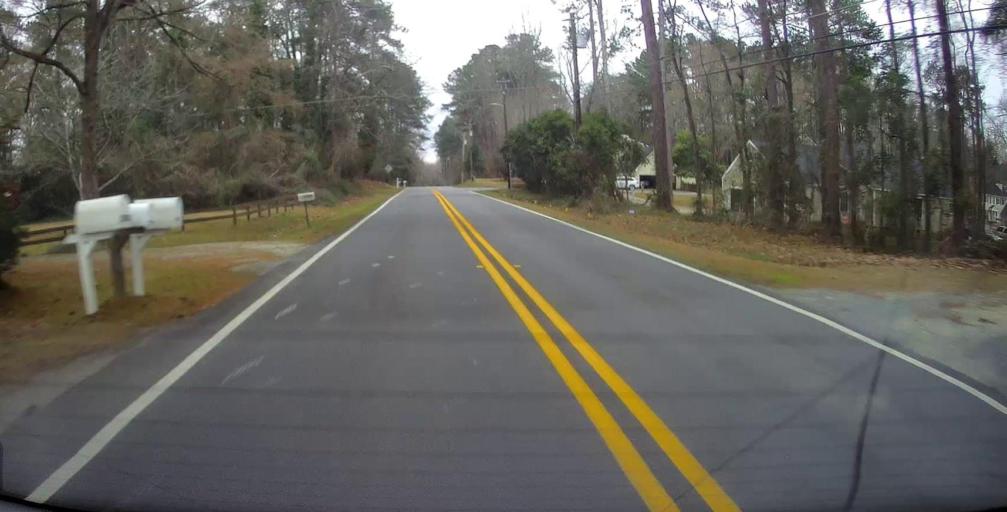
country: US
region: Georgia
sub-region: Bibb County
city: Macon
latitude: 32.8966
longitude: -83.7316
